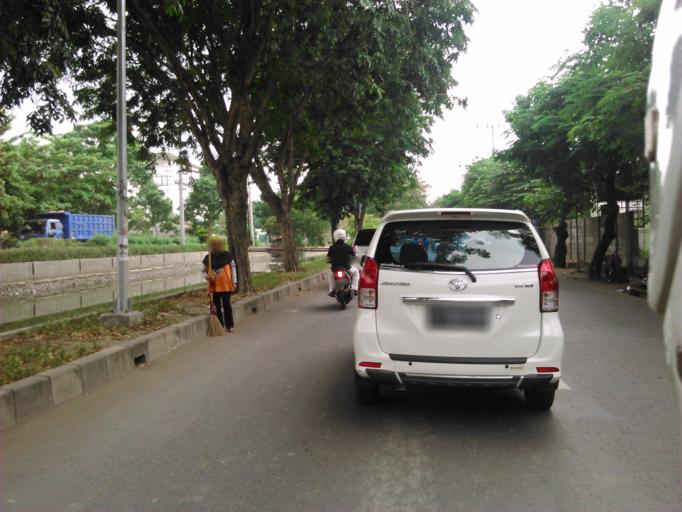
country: ID
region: East Java
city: Semampir
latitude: -7.2906
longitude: 112.7905
